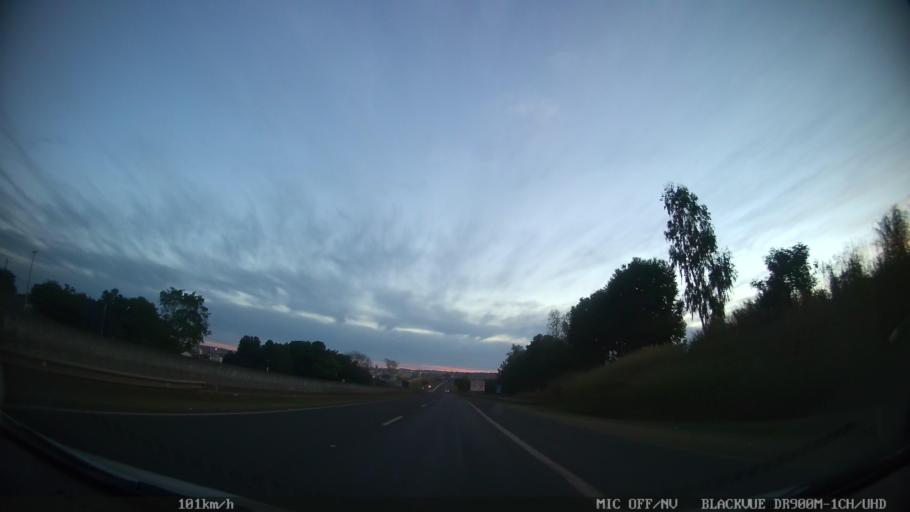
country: BR
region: Sao Paulo
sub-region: Catanduva
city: Catanduva
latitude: -21.1123
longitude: -48.9710
